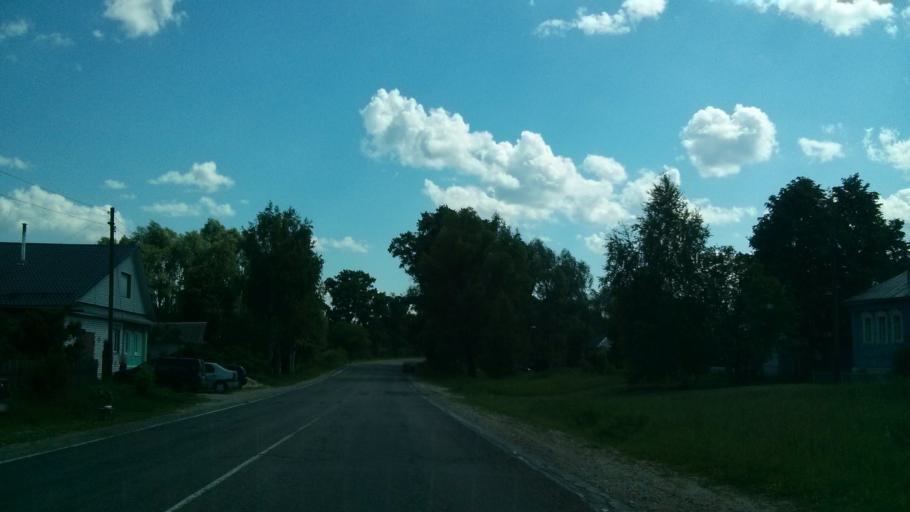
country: RU
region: Vladimir
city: Murom
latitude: 55.4745
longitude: 41.8912
